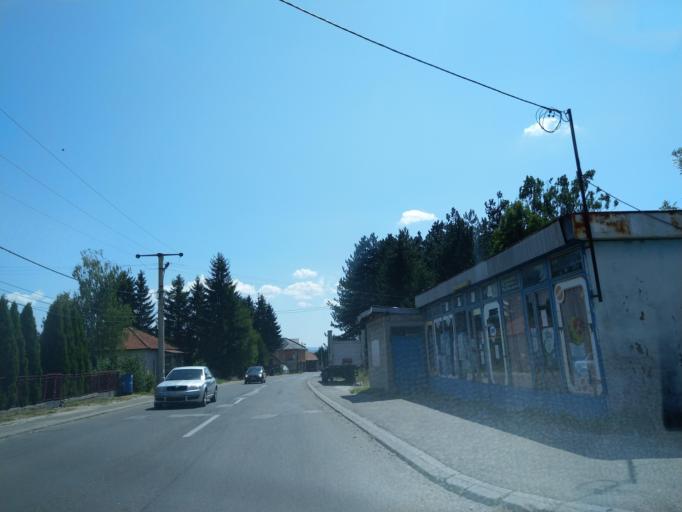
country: RS
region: Central Serbia
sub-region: Zlatiborski Okrug
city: Sjenica
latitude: 43.2765
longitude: 19.9947
